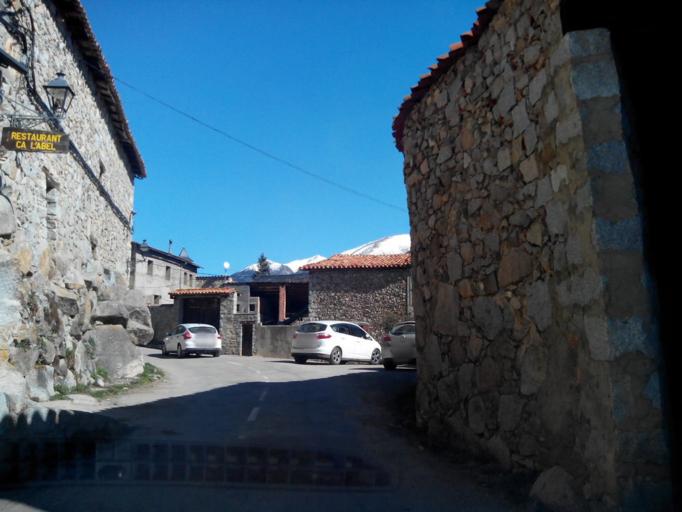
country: ES
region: Catalonia
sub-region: Provincia de Lleida
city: Lles de Cerdanya
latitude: 42.3895
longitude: 1.6878
